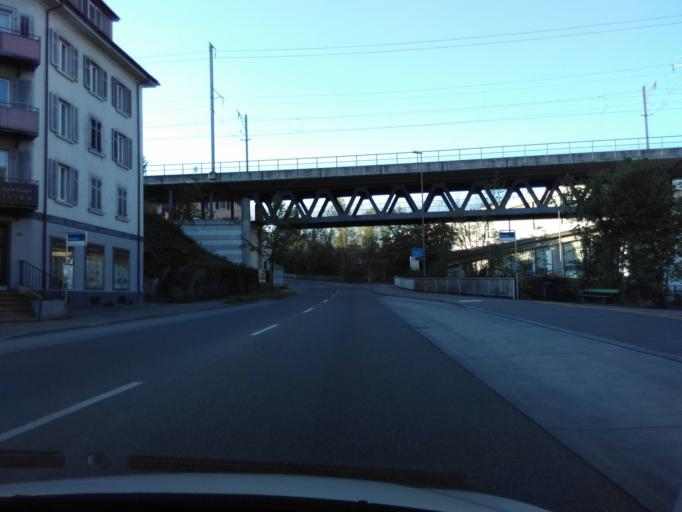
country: CH
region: Zurich
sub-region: Bezirk Hinwil
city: Tann / Tann (Dorfkern)
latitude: 47.2605
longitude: 8.8515
